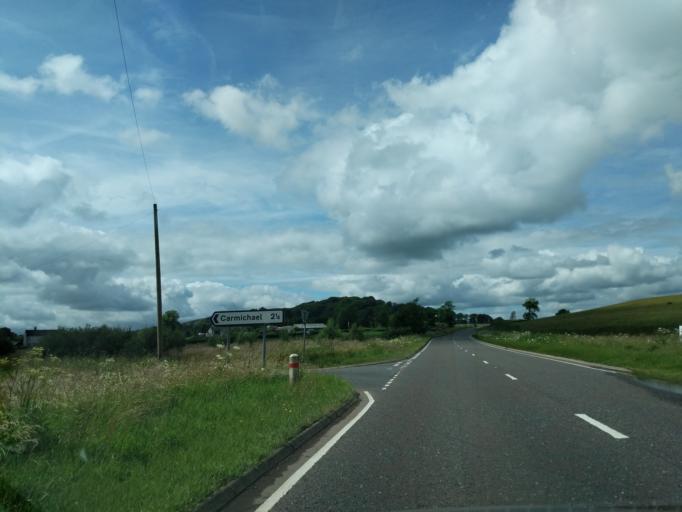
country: GB
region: Scotland
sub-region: South Lanarkshire
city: Carnwath
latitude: 55.6309
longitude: -3.6662
